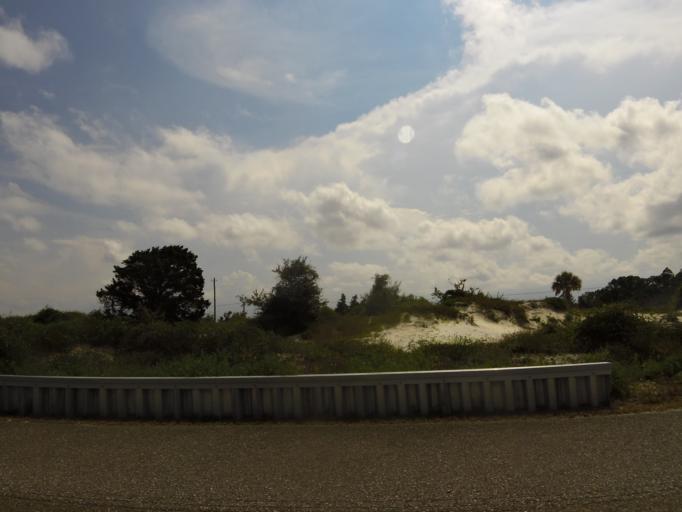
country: US
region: Florida
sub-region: Duval County
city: Atlantic Beach
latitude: 30.4372
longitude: -81.4135
